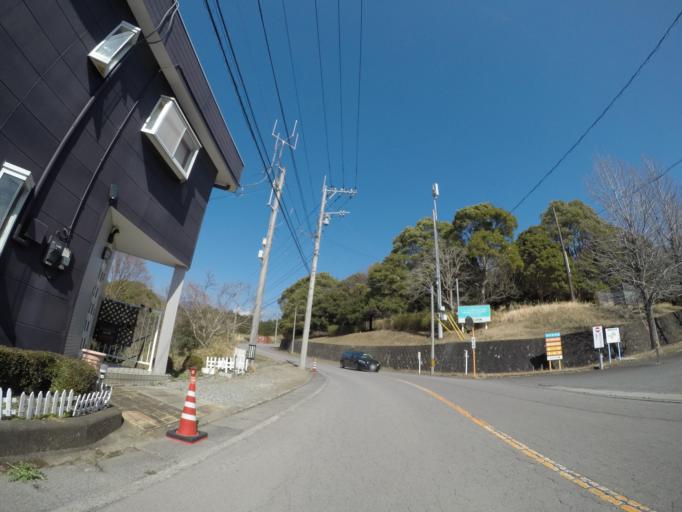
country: JP
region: Shizuoka
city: Numazu
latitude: 35.1458
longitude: 138.8373
